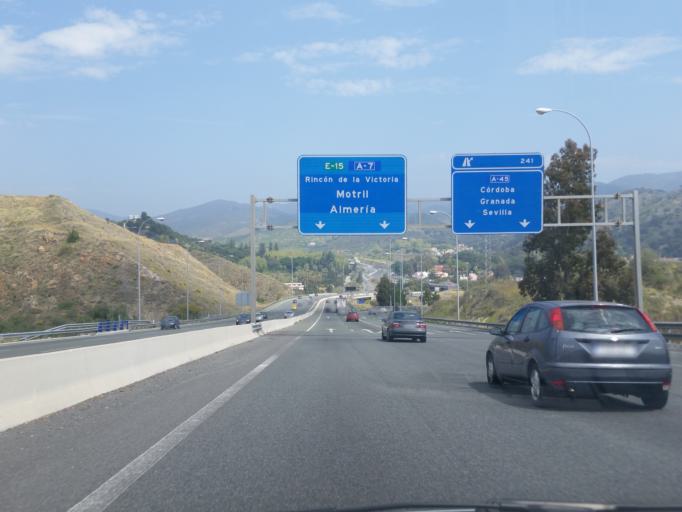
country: ES
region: Andalusia
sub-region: Provincia de Malaga
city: Malaga
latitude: 36.7515
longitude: -4.4312
